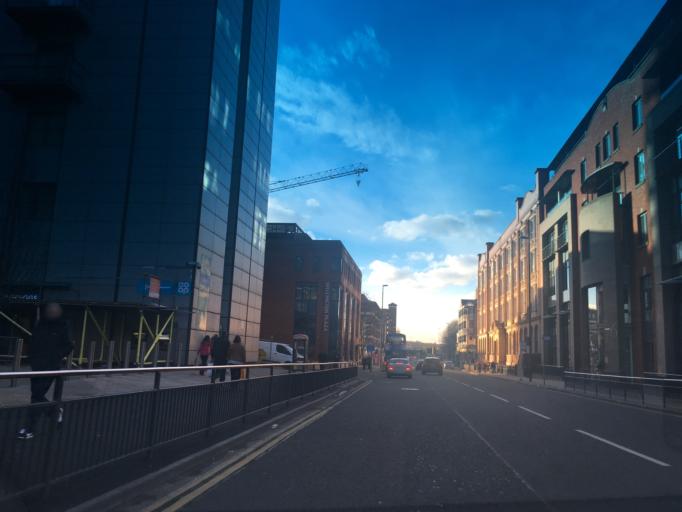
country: GB
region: England
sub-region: City and Borough of Leeds
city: Leeds
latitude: 53.7965
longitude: -1.5526
